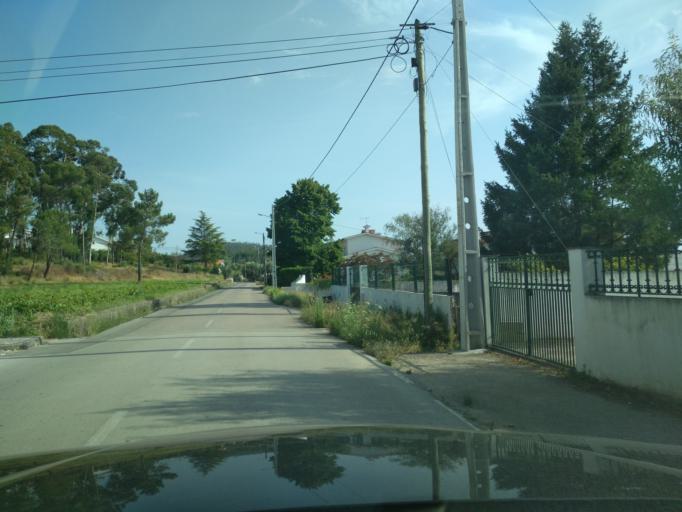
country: PT
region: Coimbra
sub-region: Condeixa-A-Nova
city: Condeixa-a-Nova
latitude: 40.1354
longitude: -8.4676
